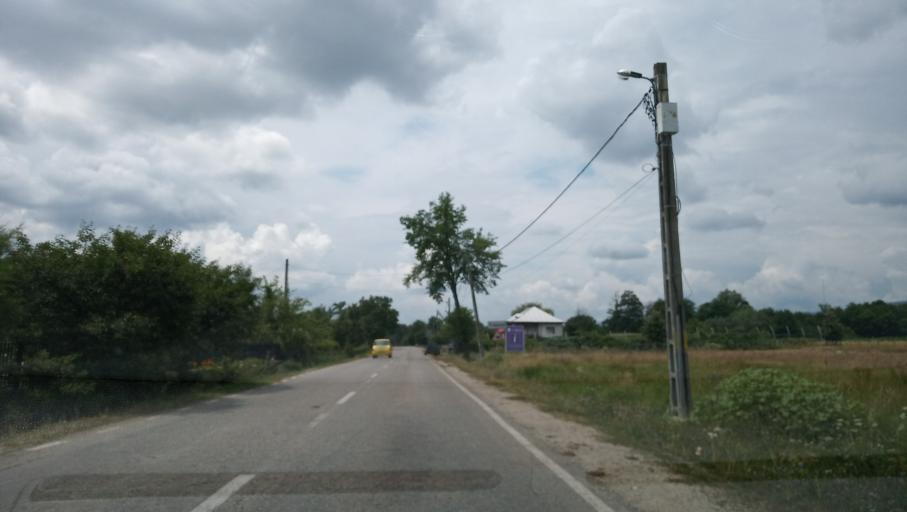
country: RO
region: Gorj
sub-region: Comuna Runcu
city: Valea Mare
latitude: 45.0852
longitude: 23.0715
